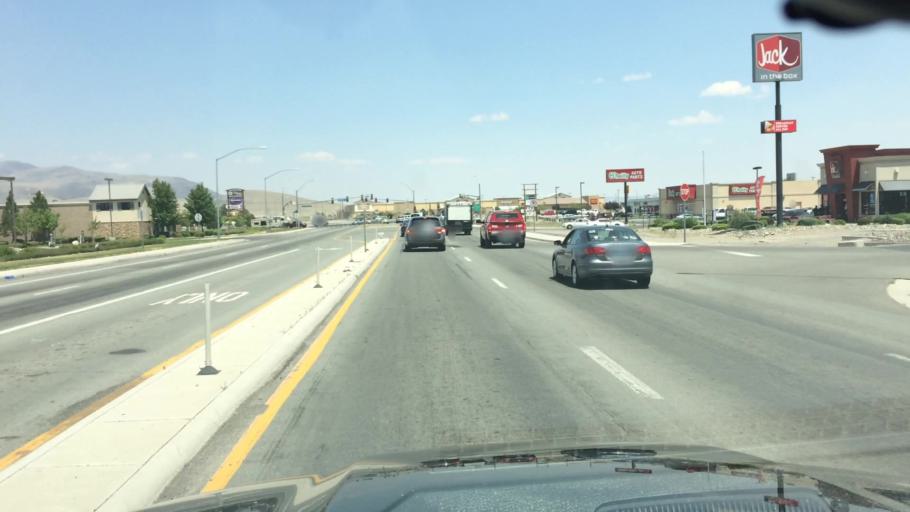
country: US
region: Nevada
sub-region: Lyon County
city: Fernley
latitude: 39.6080
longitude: -119.2219
